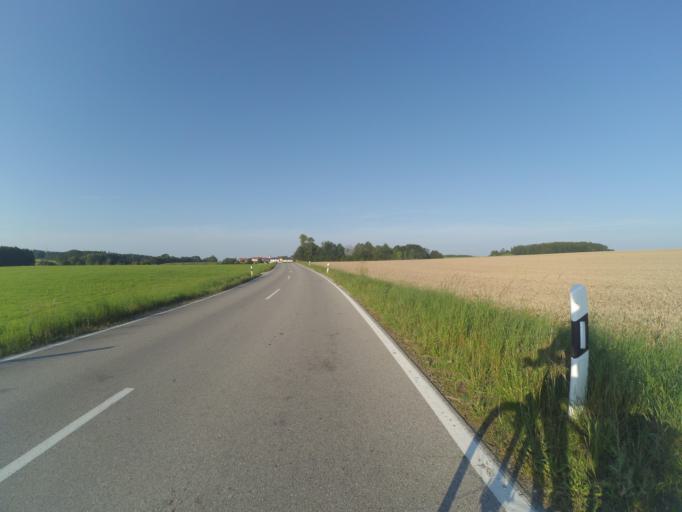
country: DE
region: Bavaria
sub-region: Swabia
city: Bad Worishofen
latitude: 48.0136
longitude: 10.5547
